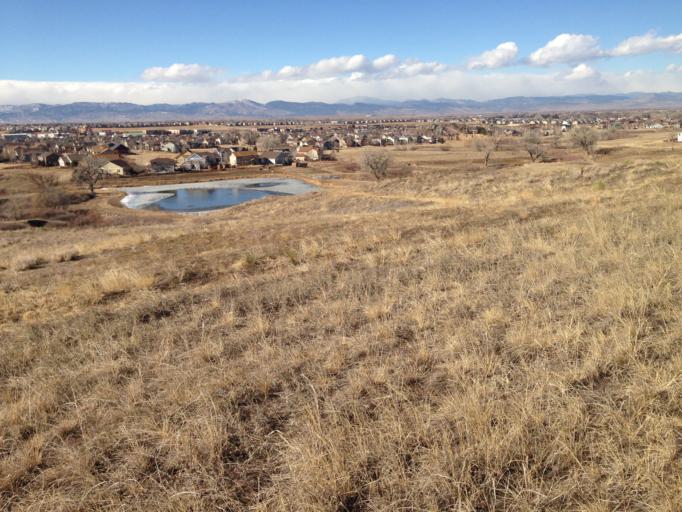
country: US
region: Colorado
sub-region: Boulder County
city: Erie
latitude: 40.0298
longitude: -105.0374
